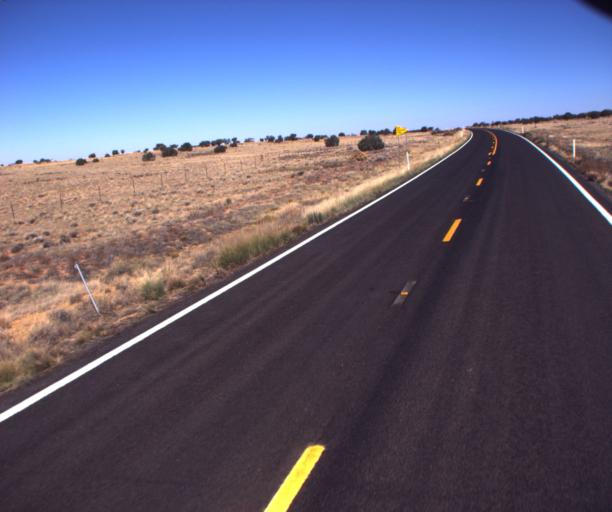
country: US
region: Arizona
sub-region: Coconino County
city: Tuba City
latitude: 35.9336
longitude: -110.8530
